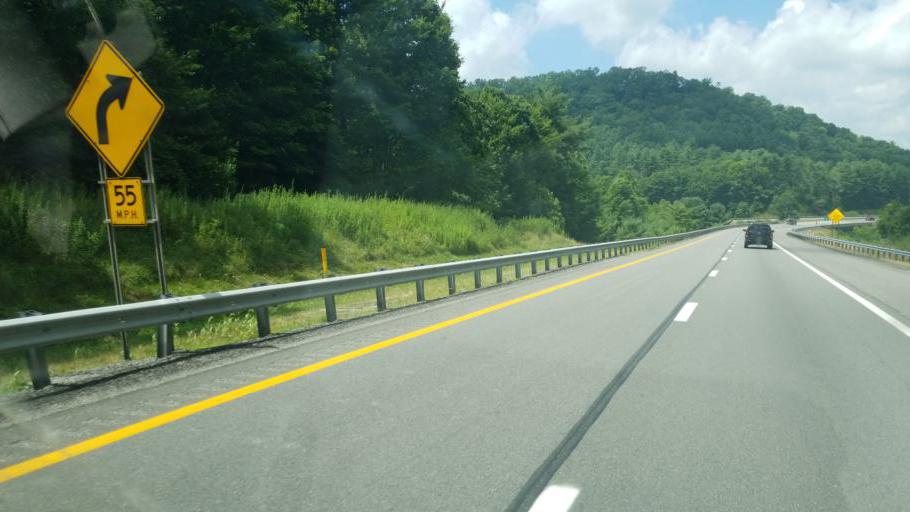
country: US
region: West Virginia
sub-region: Raleigh County
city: Beaver
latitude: 37.7086
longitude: -81.1491
